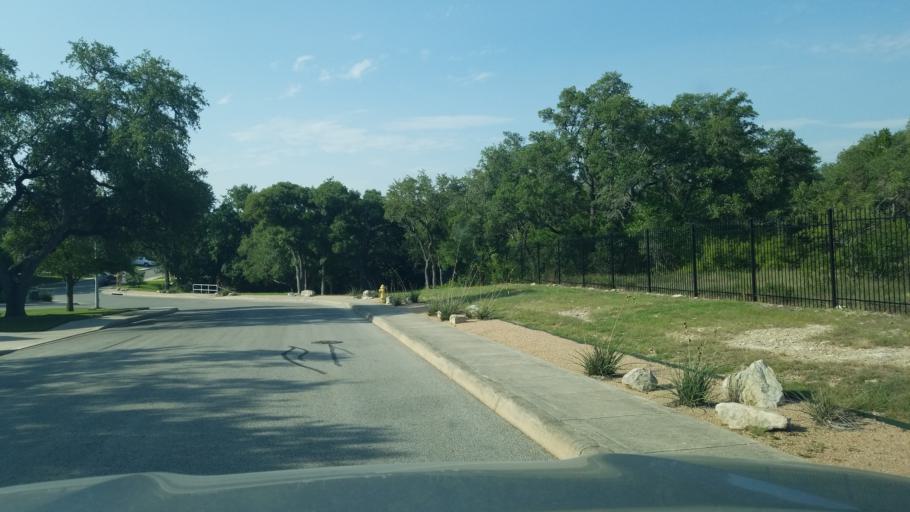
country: US
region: Texas
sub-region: Medina County
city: La Coste
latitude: 29.4413
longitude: -98.7538
